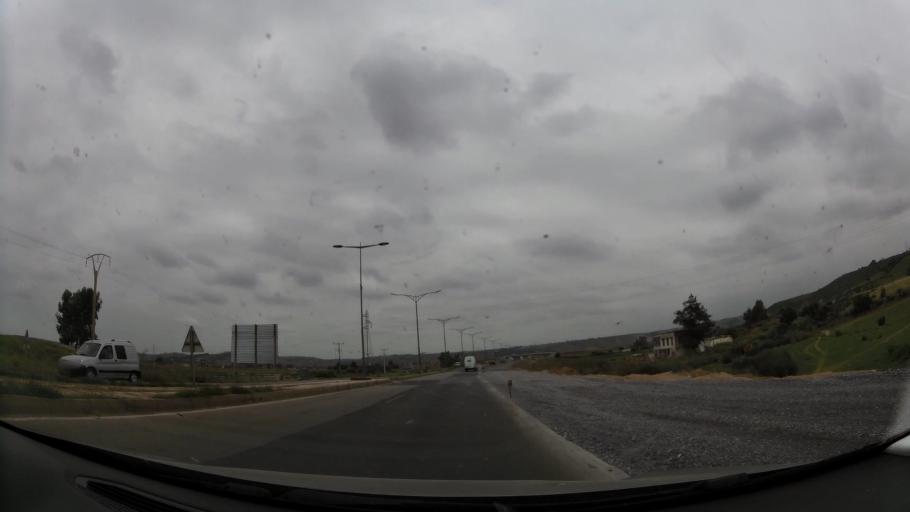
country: MA
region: Rabat-Sale-Zemmour-Zaer
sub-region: Rabat
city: Rabat
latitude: 33.9849
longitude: -6.7980
